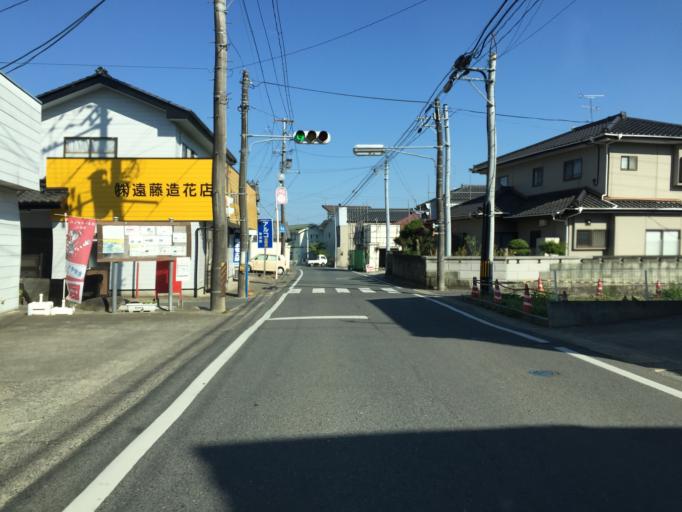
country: JP
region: Ibaraki
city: Kitaibaraki
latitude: 36.8928
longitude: 140.7566
